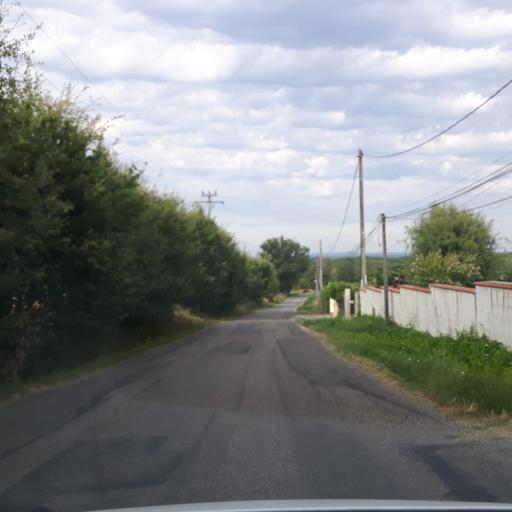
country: FR
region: Midi-Pyrenees
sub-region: Departement de la Haute-Garonne
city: Castelnau-d'Estretefonds
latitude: 43.8120
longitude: 1.3527
